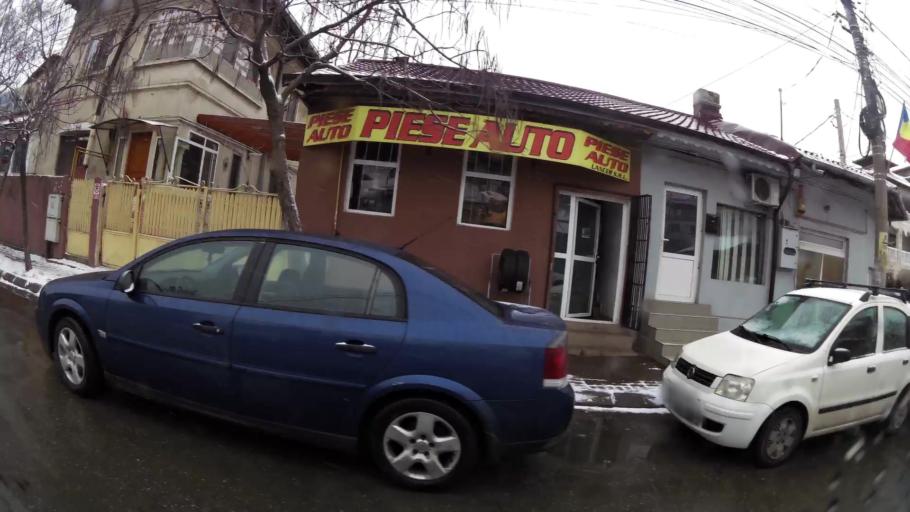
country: RO
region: Dambovita
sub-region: Municipiul Targoviste
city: Targoviste
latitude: 44.9224
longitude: 25.4737
